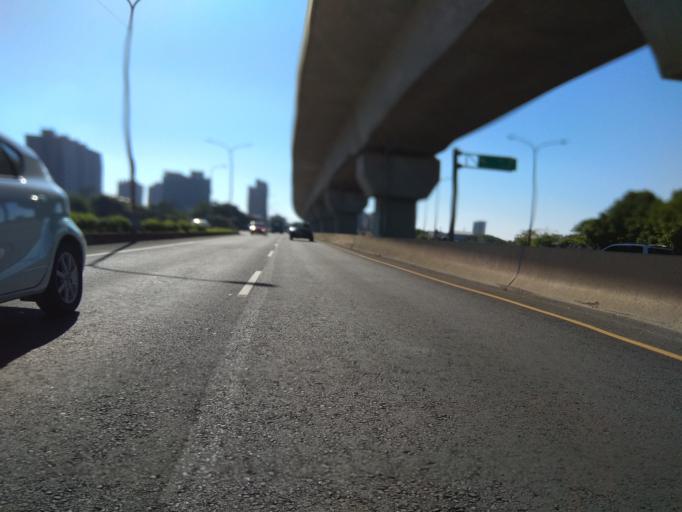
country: TW
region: Taiwan
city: Taoyuan City
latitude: 24.9661
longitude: 121.1681
